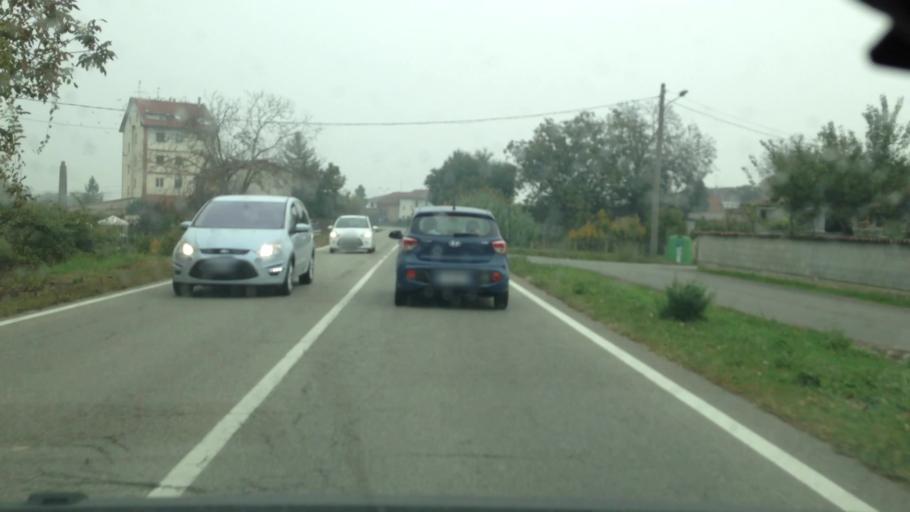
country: IT
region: Piedmont
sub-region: Provincia di Alessandria
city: Felizzano
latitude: 44.9004
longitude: 8.4417
